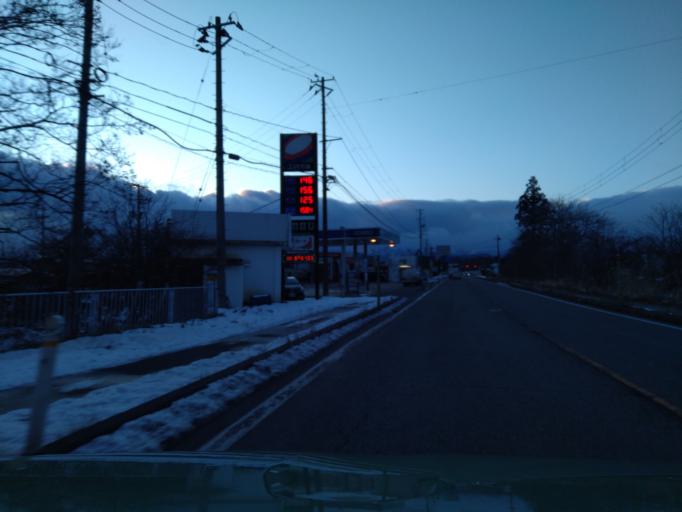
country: JP
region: Iwate
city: Shizukuishi
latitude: 39.6889
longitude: 140.9968
